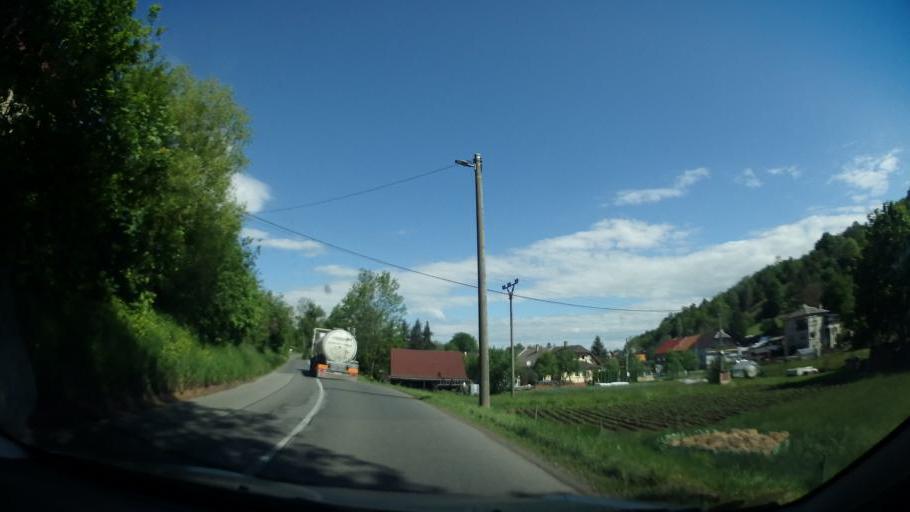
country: CZ
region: Pardubicky
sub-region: Okres Svitavy
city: Moravska Trebova
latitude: 49.7103
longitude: 16.6396
